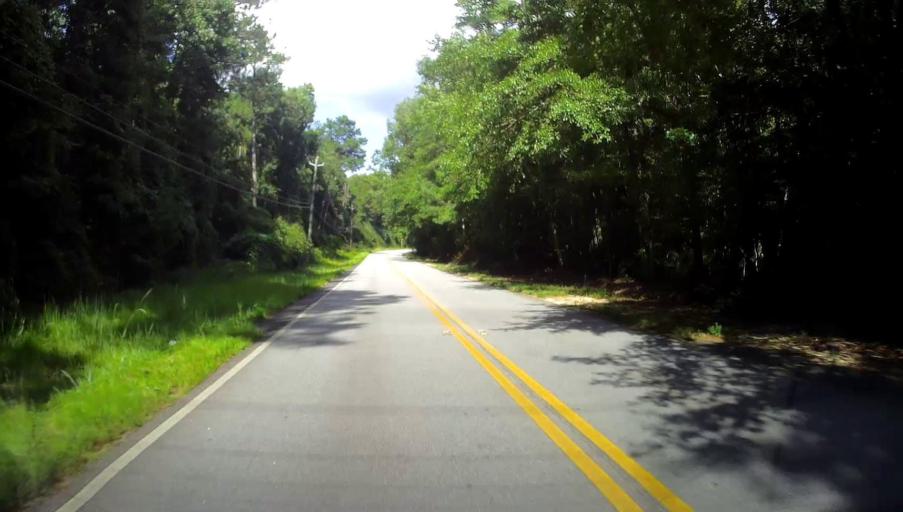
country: US
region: Georgia
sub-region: Muscogee County
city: Columbus
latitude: 32.5668
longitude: -84.8452
